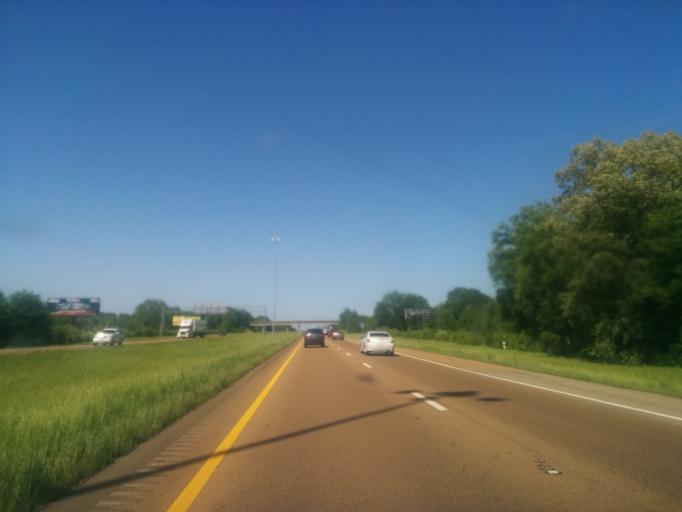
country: US
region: Mississippi
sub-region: Madison County
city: Canton
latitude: 32.5467
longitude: -90.0912
